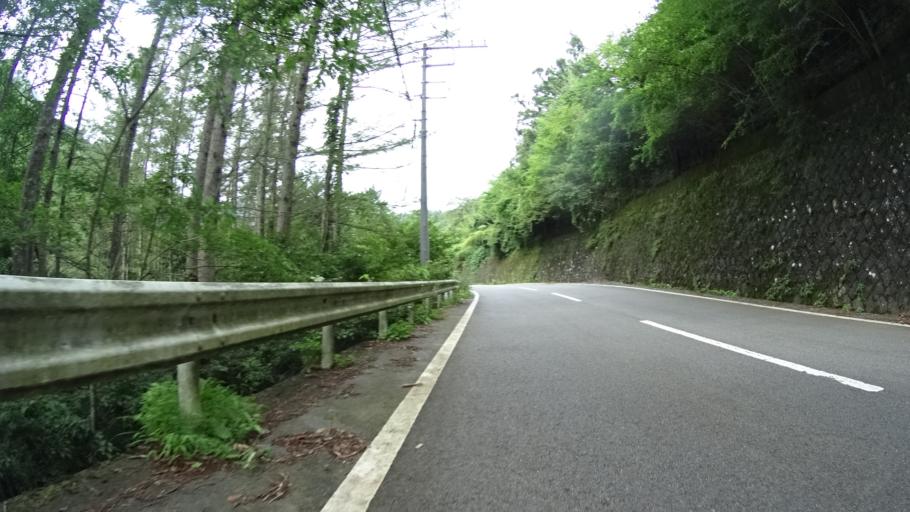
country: JP
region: Yamanashi
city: Kofu-shi
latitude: 35.7686
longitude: 138.5499
